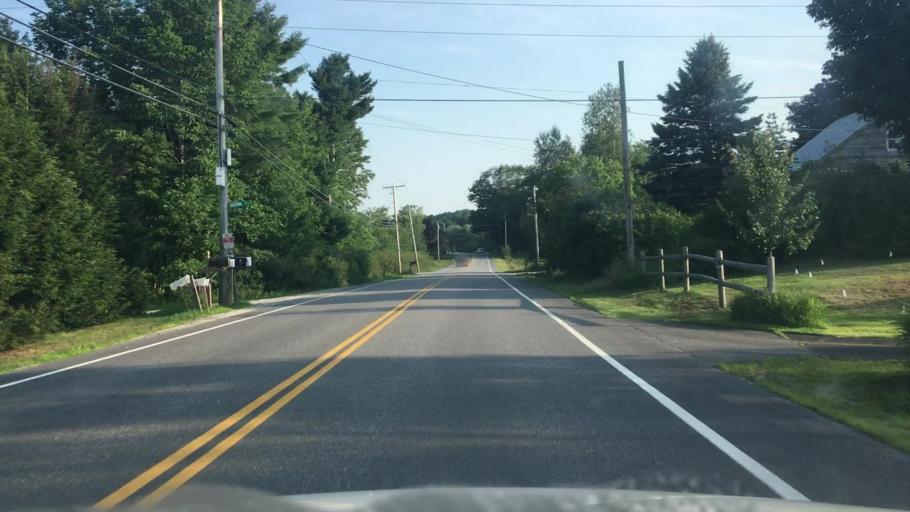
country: US
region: Maine
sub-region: Cumberland County
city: Freeport
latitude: 43.8977
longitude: -70.0943
